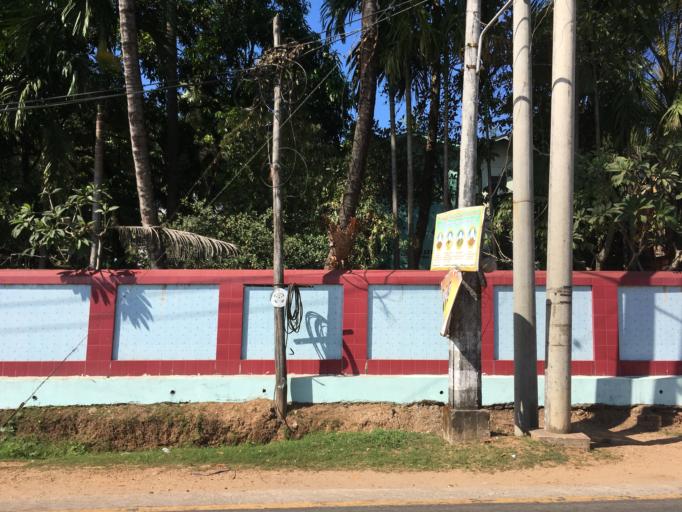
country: MM
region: Mon
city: Mawlamyine
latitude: 16.4883
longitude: 97.6304
